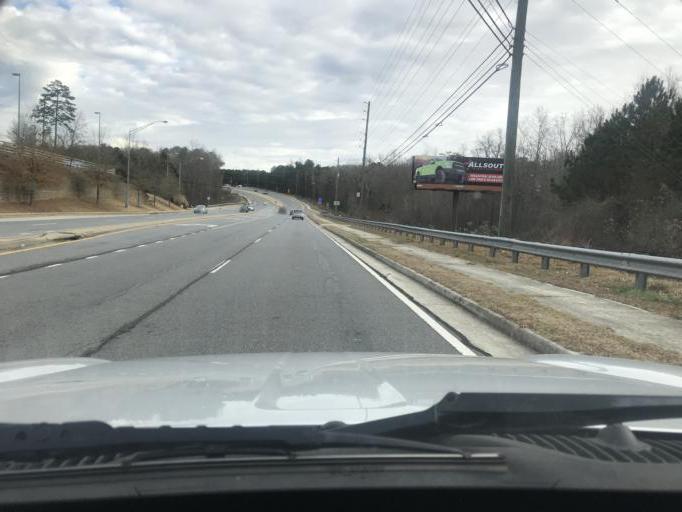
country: US
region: Georgia
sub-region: Gwinnett County
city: Buford
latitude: 34.0713
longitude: -83.9752
